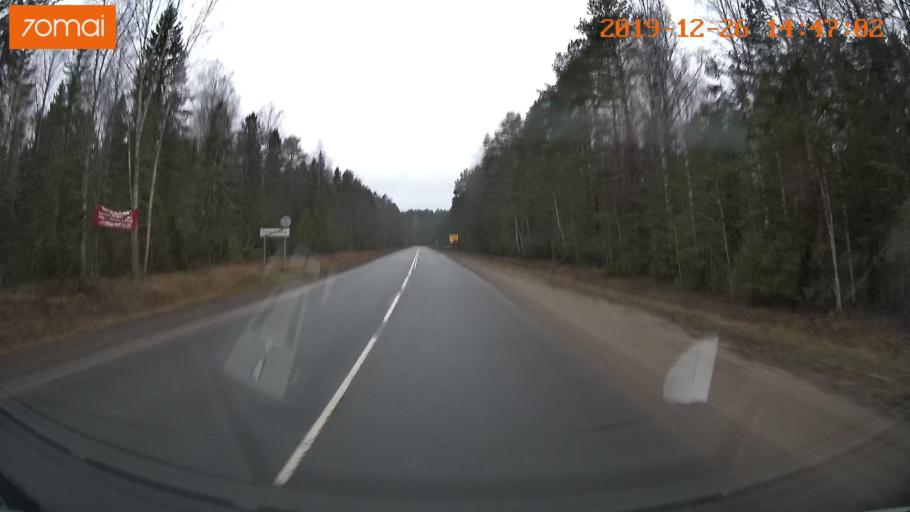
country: RU
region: Jaroslavl
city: Poshekhon'ye
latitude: 58.3413
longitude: 39.0075
